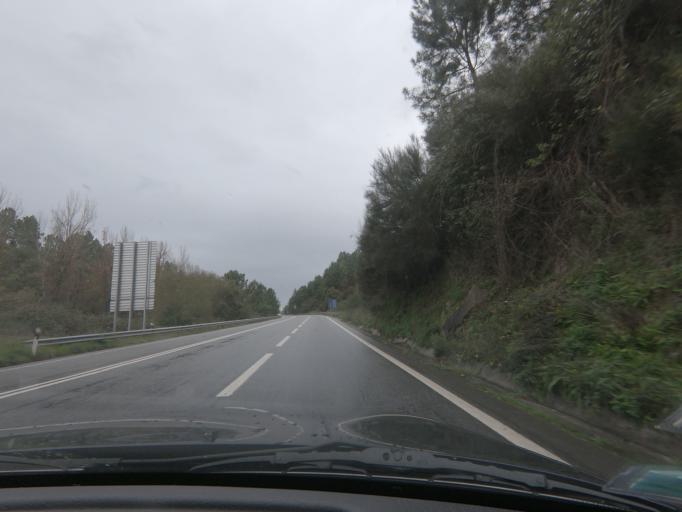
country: PT
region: Porto
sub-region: Amarante
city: Teloes
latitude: 41.3108
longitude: -8.0751
